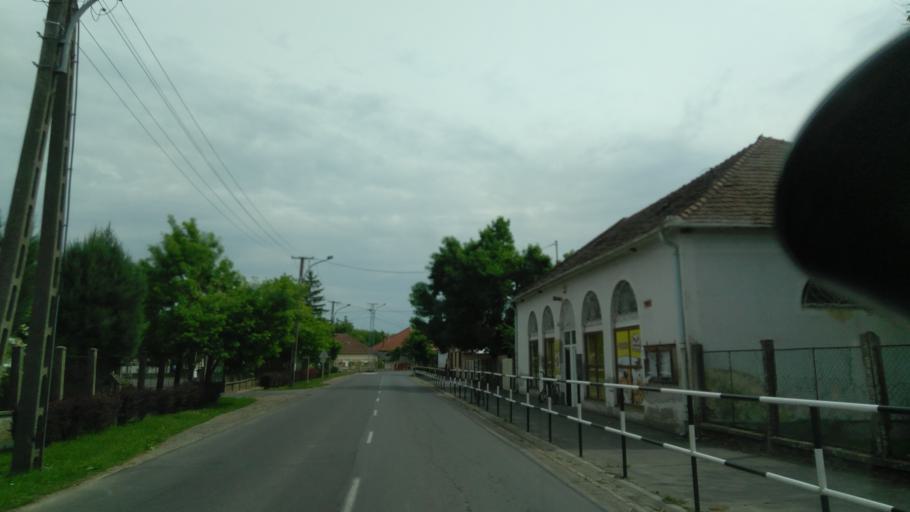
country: HU
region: Bekes
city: Sarkad
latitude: 46.8096
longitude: 21.3818
